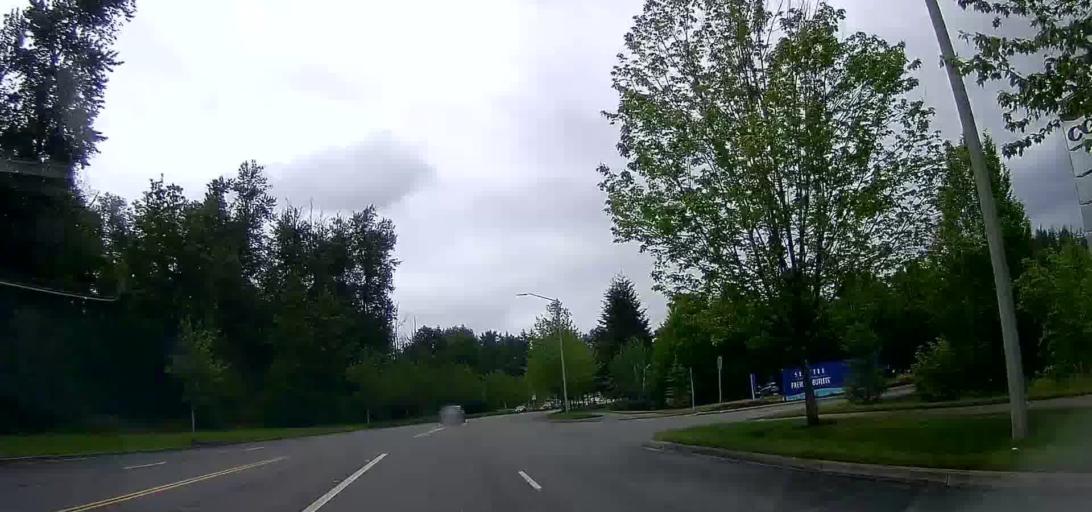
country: US
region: Washington
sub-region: Snohomish County
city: Marysville
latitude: 48.0941
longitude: -122.1908
